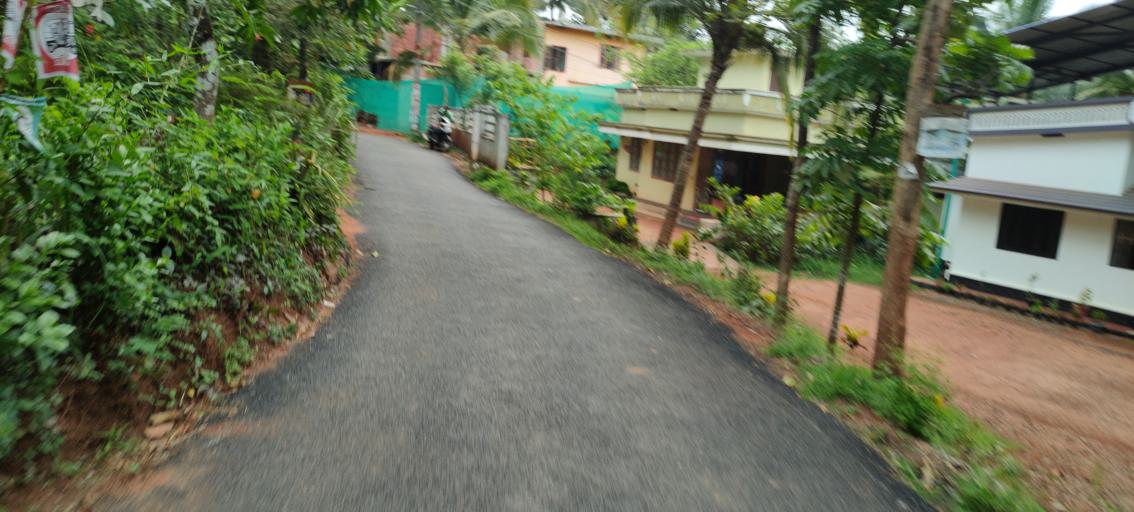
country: IN
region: Kerala
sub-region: Malappuram
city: Ponnani
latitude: 10.7746
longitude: 76.0313
